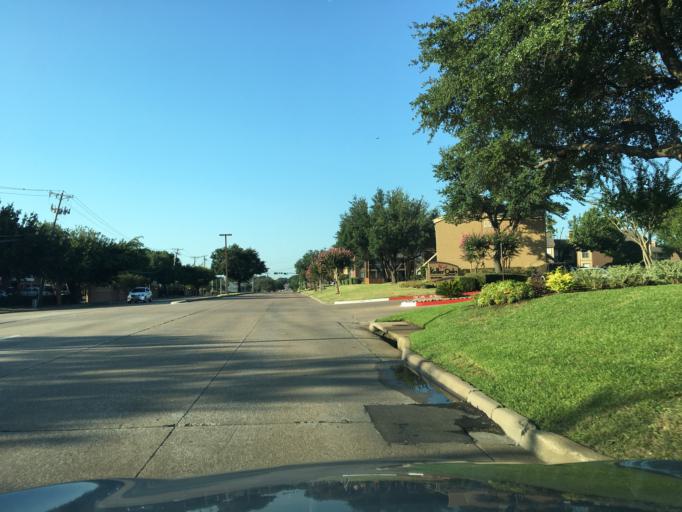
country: US
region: Texas
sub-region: Dallas County
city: Addison
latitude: 32.9681
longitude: -96.8537
